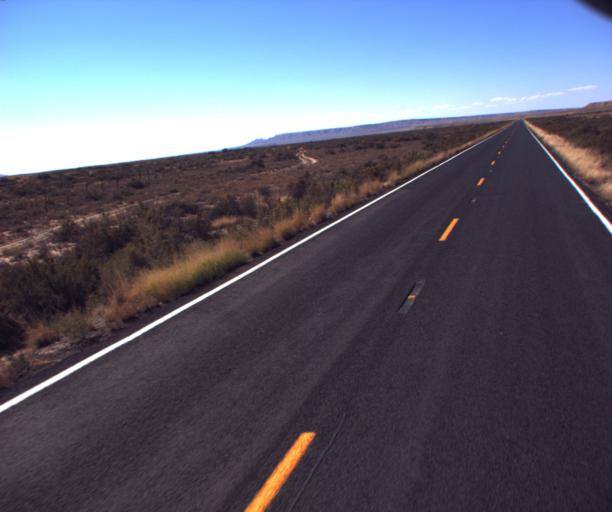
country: US
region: Arizona
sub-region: Navajo County
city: First Mesa
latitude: 35.9834
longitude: -110.7149
